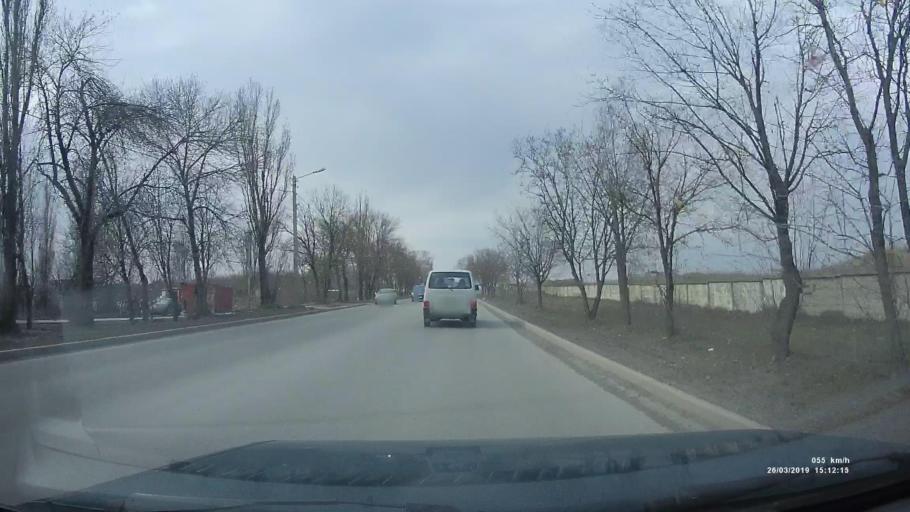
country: RU
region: Rostov
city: Taganrog
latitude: 47.2662
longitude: 38.8640
